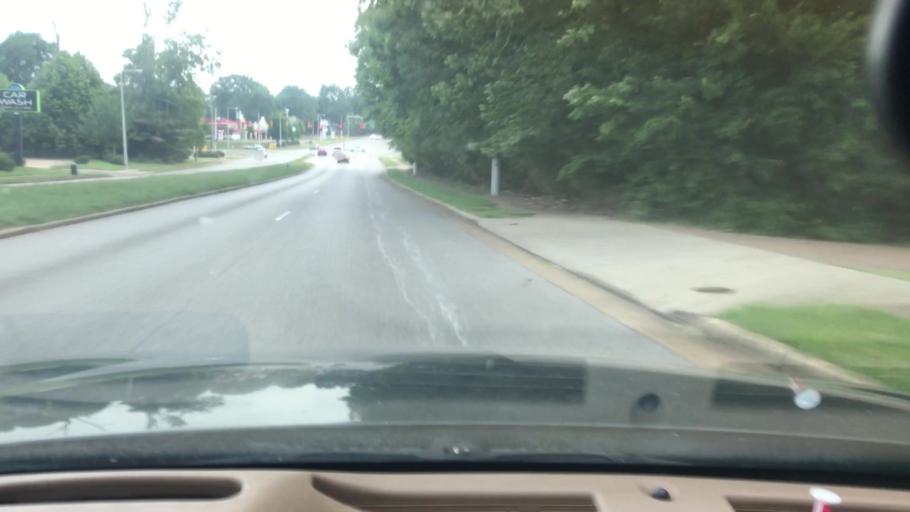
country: US
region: Tennessee
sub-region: Shelby County
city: Bartlett
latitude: 35.1810
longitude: -89.8714
